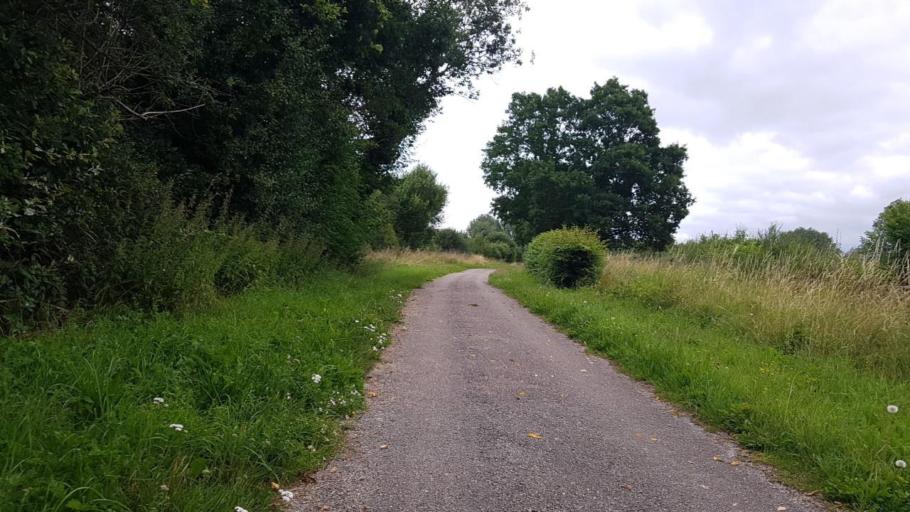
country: FR
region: Picardie
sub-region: Departement de l'Aisne
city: Origny-en-Thierache
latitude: 49.9258
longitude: 3.9753
